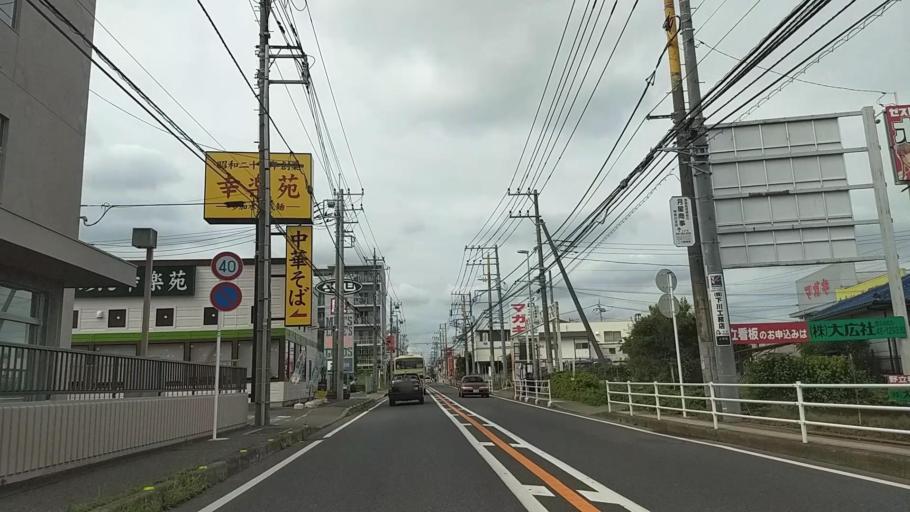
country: JP
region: Kanagawa
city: Minami-rinkan
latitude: 35.4568
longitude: 139.4670
